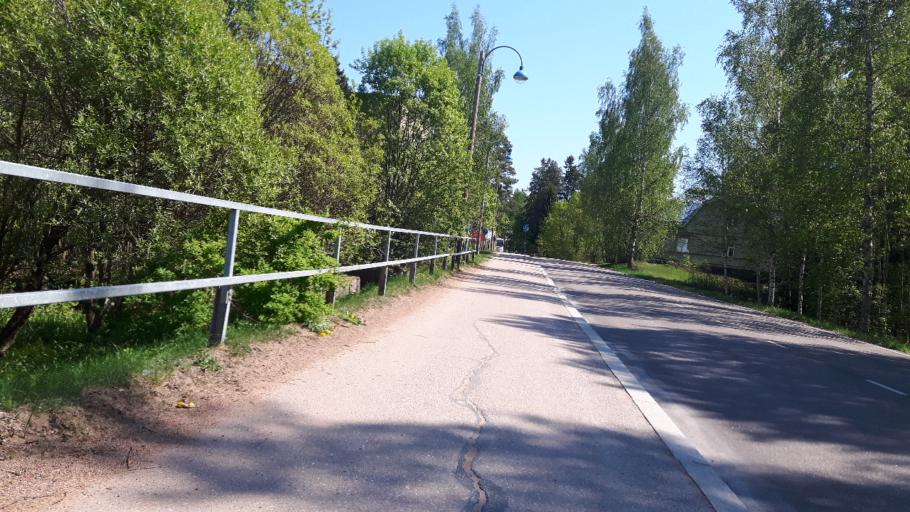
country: FI
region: Kymenlaakso
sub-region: Kotka-Hamina
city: Pyhtaeae
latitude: 60.4914
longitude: 26.5468
